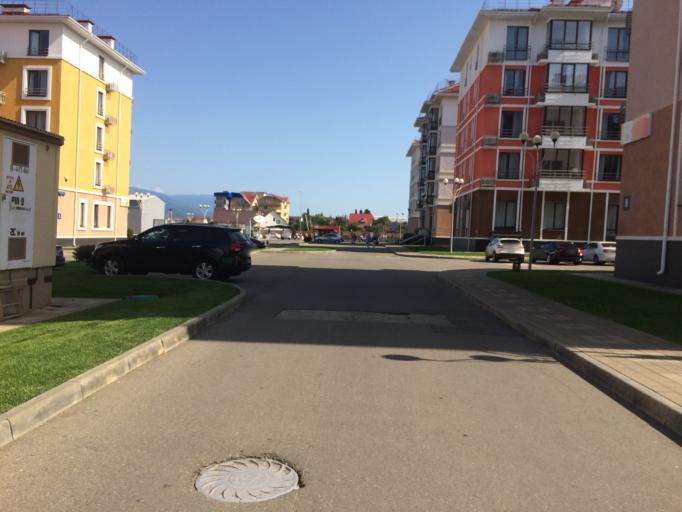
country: RU
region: Krasnodarskiy
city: Adler
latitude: 43.3962
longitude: 39.9779
